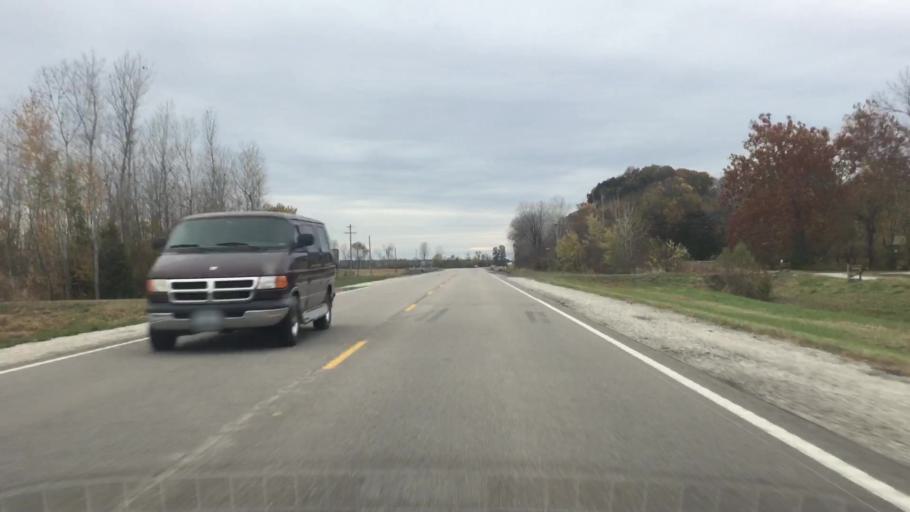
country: US
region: Missouri
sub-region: Callaway County
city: Holts Summit
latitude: 38.5828
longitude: -92.1095
